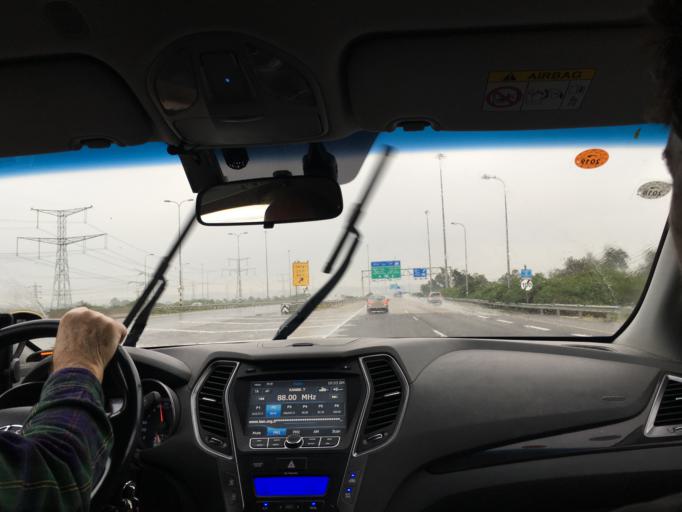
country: IL
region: Central District
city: Rosh Ha'Ayin
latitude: 32.1164
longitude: 34.9270
